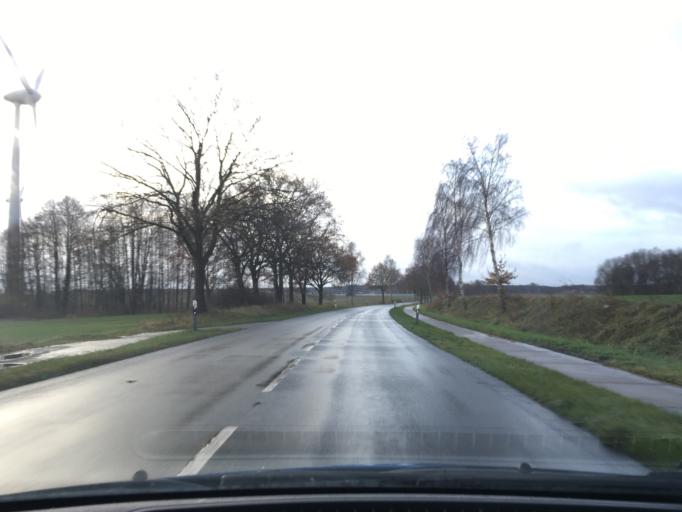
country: DE
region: Lower Saxony
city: Embsen
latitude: 53.1922
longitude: 10.3473
